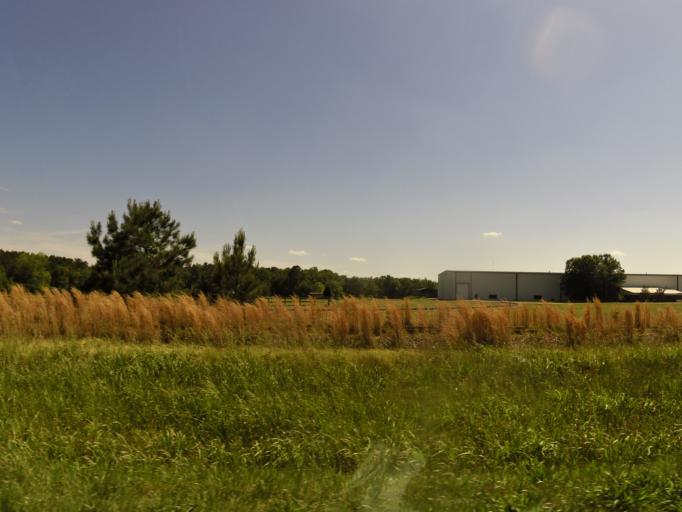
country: US
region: South Carolina
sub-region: Aiken County
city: Aiken
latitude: 33.5227
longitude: -81.6134
